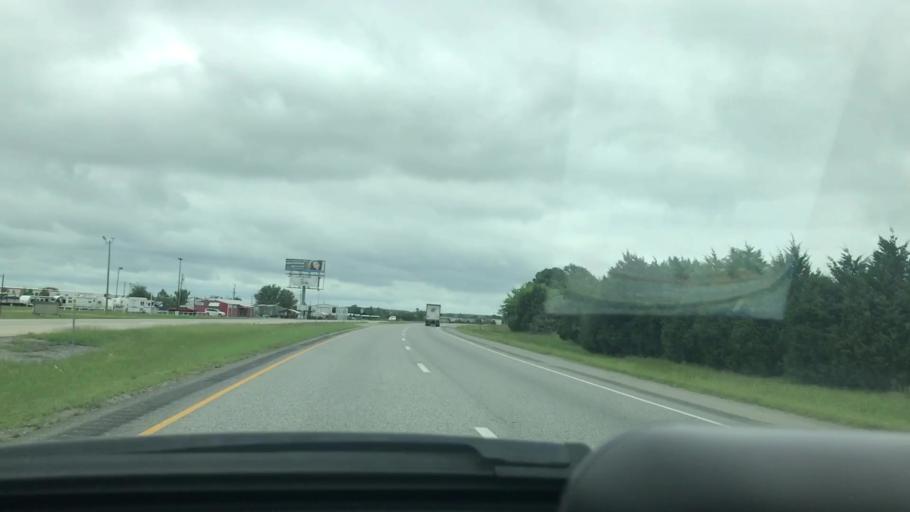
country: US
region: Oklahoma
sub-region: Pittsburg County
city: McAlester
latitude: 34.7311
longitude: -95.8992
